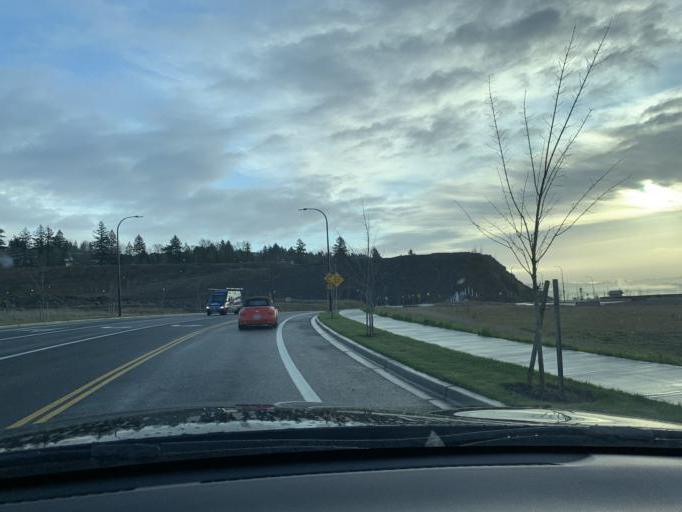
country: US
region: Washington
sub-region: Clark County
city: Mill Plain
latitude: 45.5868
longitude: -122.4726
